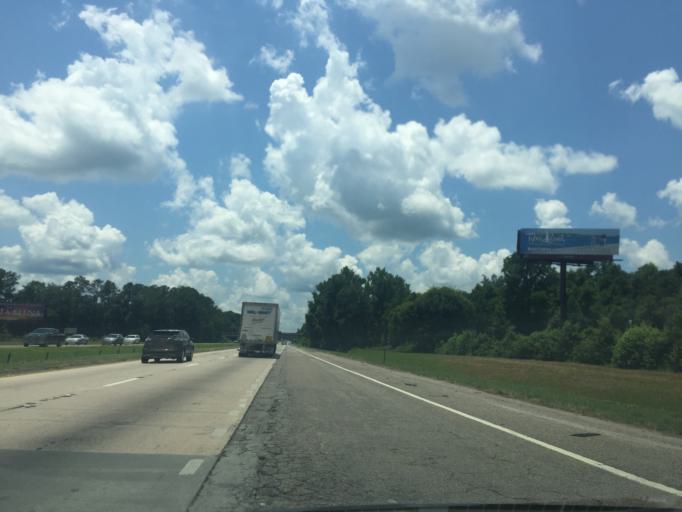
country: US
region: South Carolina
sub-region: Jasper County
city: Ridgeland
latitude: 32.4736
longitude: -80.9737
